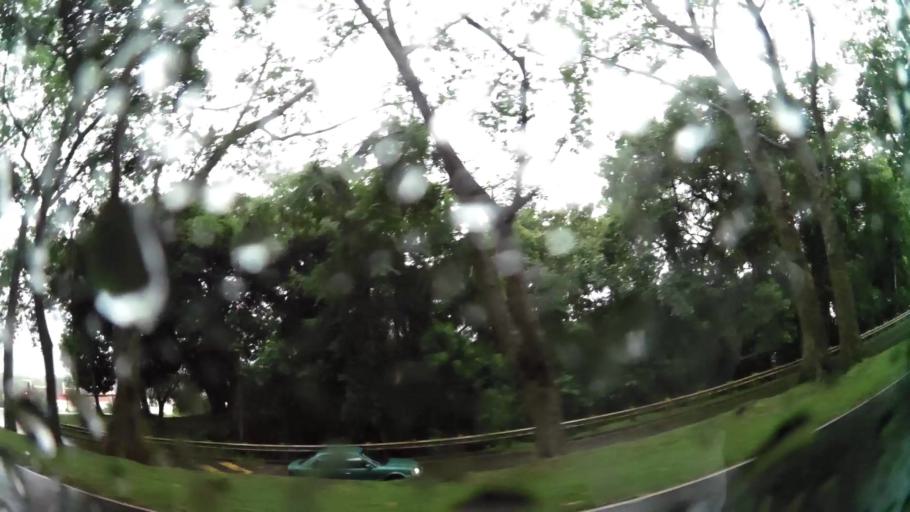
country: PA
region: Panama
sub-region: Distrito de Panama
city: Paraiso
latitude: 9.0092
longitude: -79.5956
